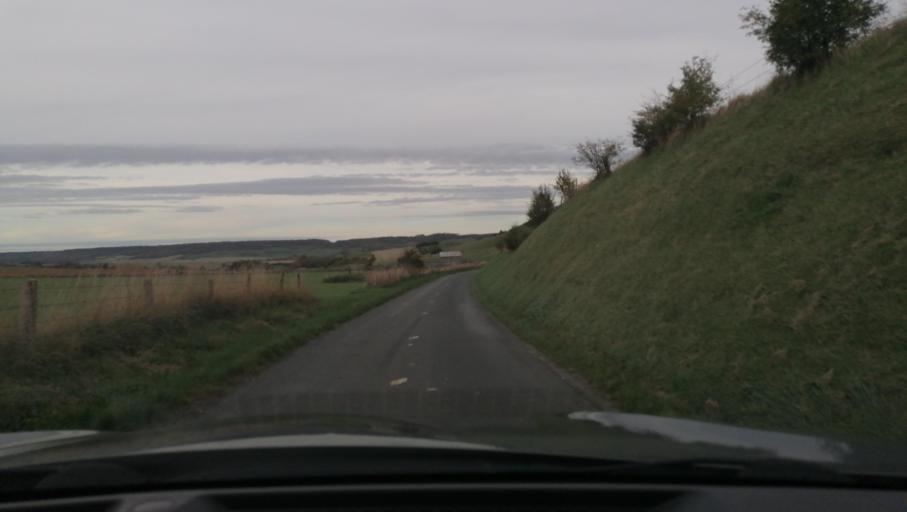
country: FR
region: Picardie
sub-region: Departement de la Somme
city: Bouttencourt
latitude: 49.8937
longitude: 1.6738
